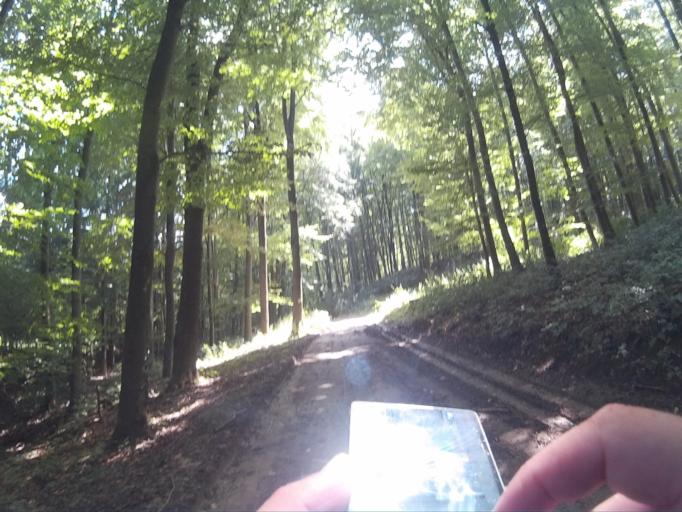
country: HU
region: Veszprem
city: Zirc
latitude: 47.2030
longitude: 17.9064
